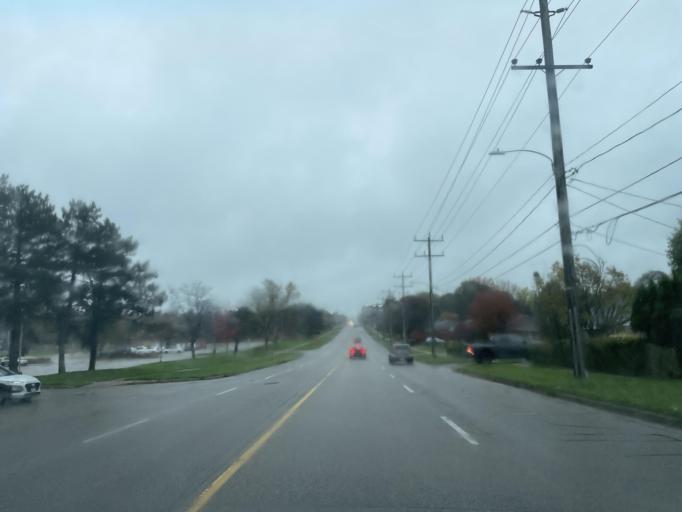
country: CA
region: Ontario
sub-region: Wellington County
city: Guelph
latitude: 43.5639
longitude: -80.2407
